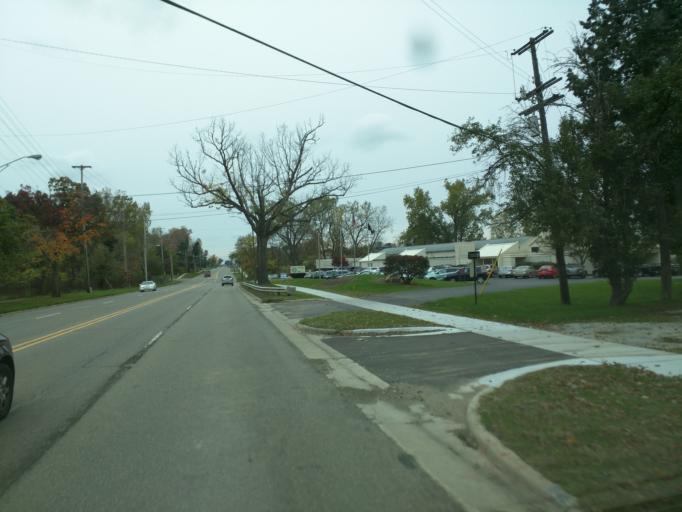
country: US
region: Michigan
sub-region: Ingham County
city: Edgemont Park
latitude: 42.7629
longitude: -84.5769
